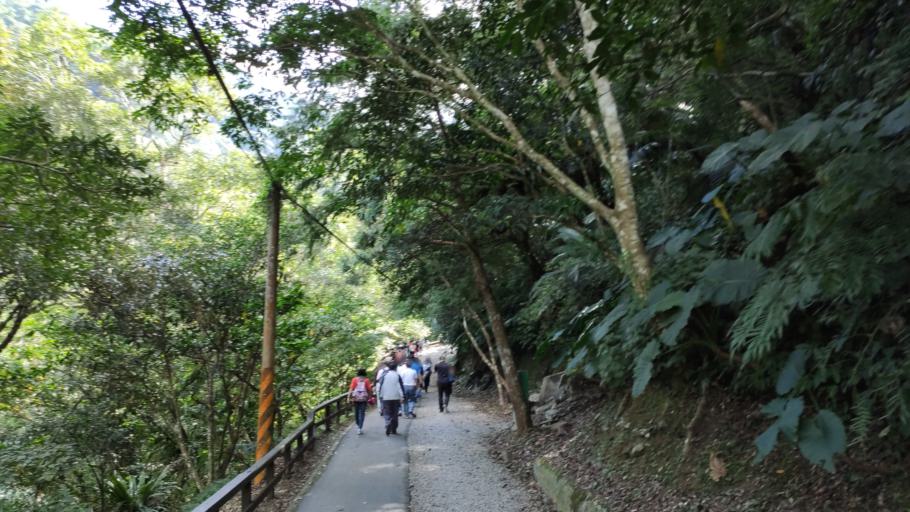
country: TW
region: Taiwan
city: Daxi
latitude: 24.8270
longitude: 121.4474
